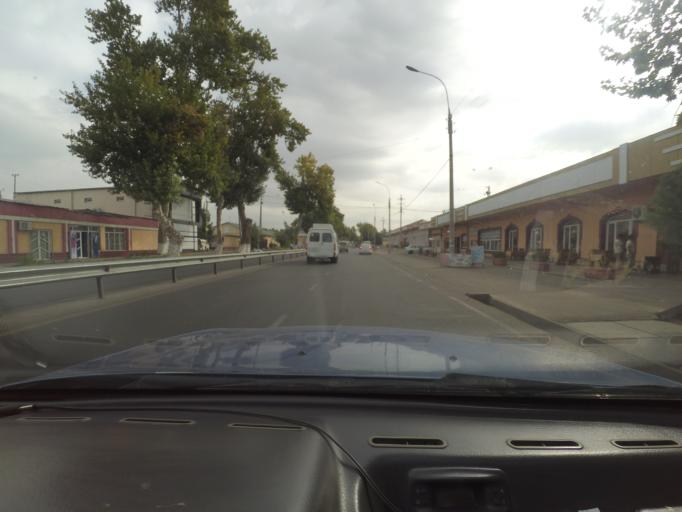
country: UZ
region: Toshkent
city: Qibray
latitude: 41.3885
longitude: 69.4608
